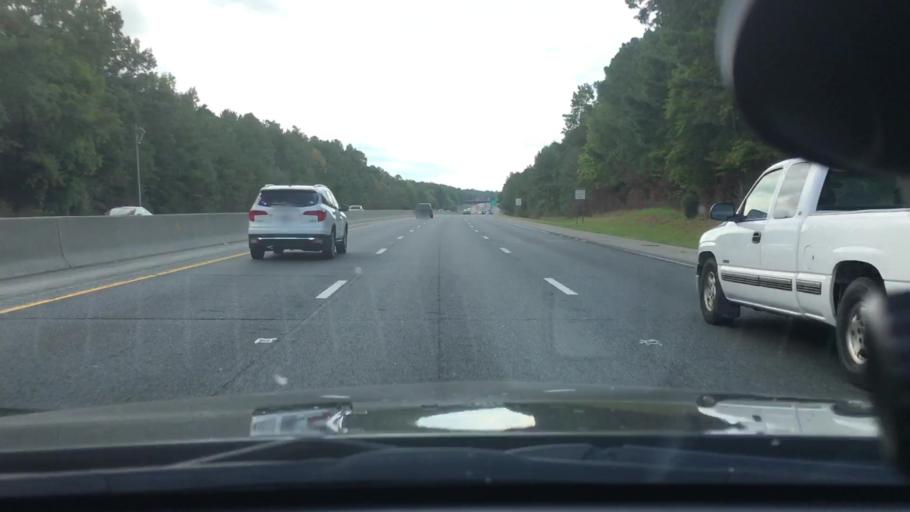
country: US
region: North Carolina
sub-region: Orange County
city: Chapel Hill
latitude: 35.9433
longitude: -78.9935
